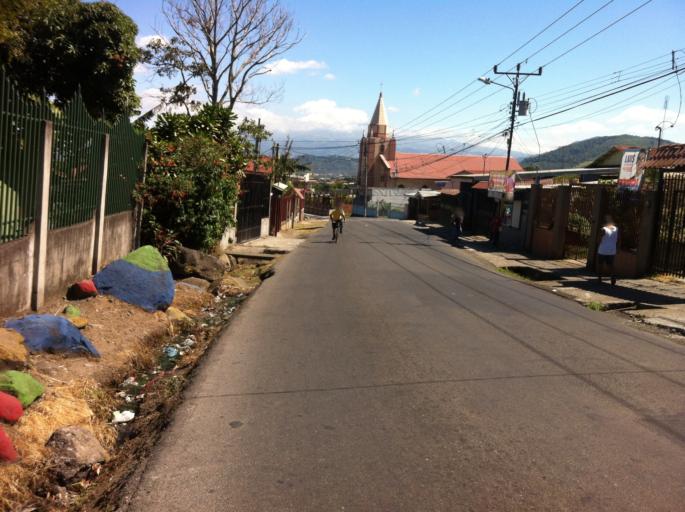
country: CR
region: San Jose
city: San Juan de Dios
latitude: 9.8784
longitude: -84.0843
